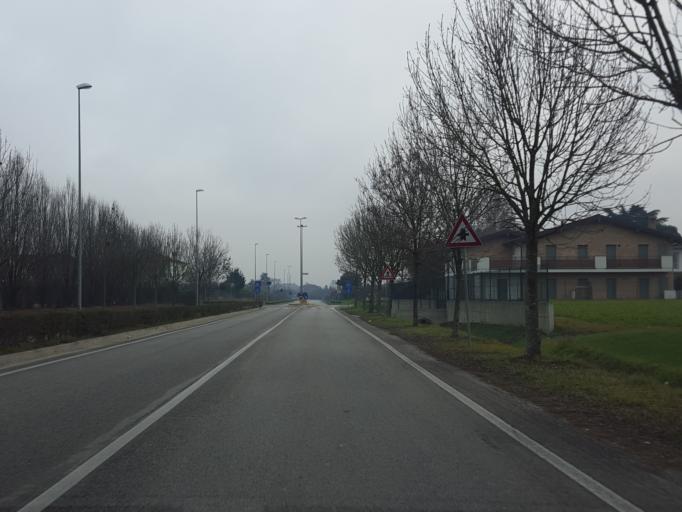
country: IT
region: Veneto
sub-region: Provincia di Vicenza
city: Vicenza
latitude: 45.5384
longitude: 11.5727
